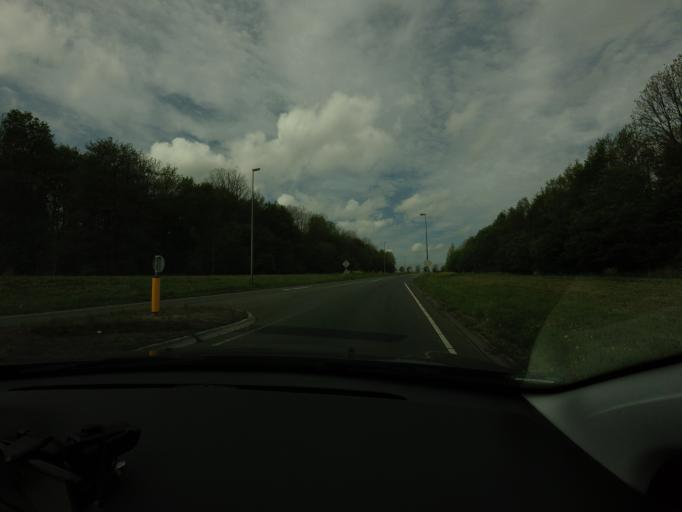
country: NL
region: North Holland
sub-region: Gemeente Beemster
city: Halfweg
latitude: 52.5055
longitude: 4.9325
